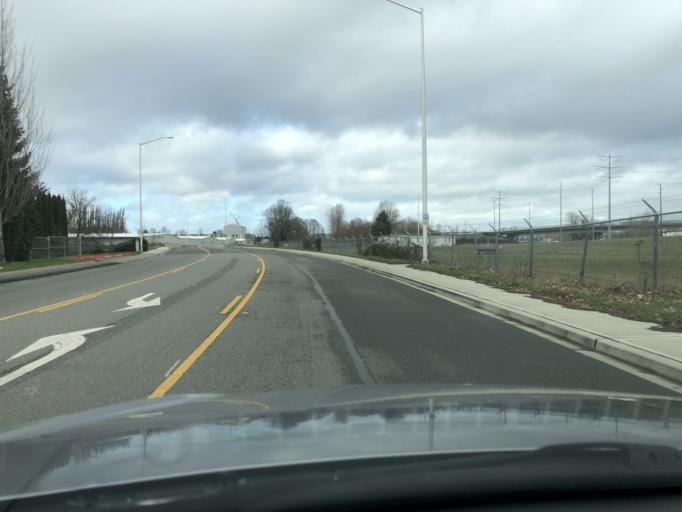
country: US
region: Washington
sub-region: King County
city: Kent
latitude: 47.4232
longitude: -122.2440
